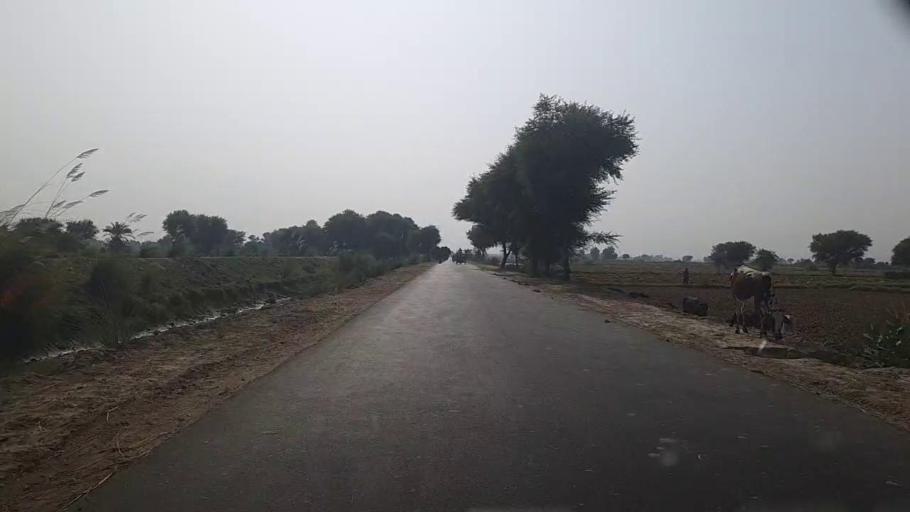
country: PK
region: Sindh
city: Kashmor
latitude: 28.4076
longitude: 69.5599
